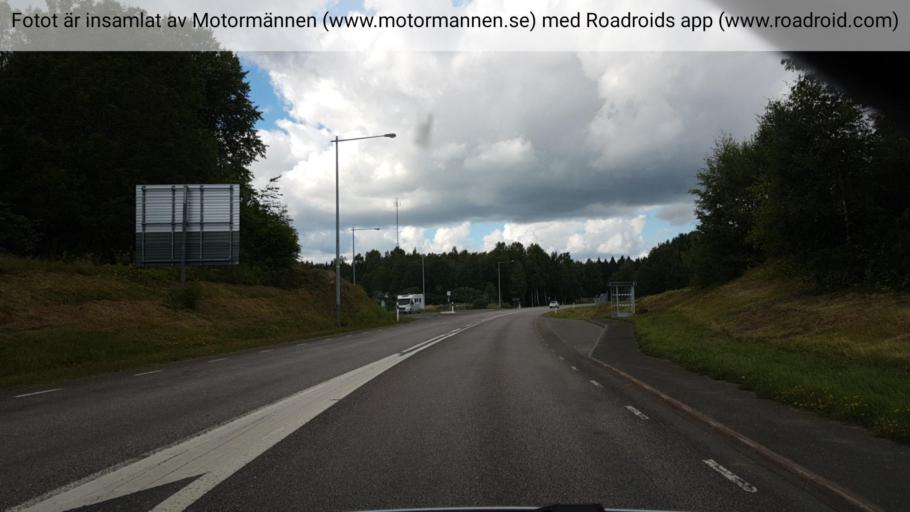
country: SE
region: Vaestra Goetaland
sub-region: Falkopings Kommun
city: Falkoeping
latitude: 58.0278
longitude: 13.5503
